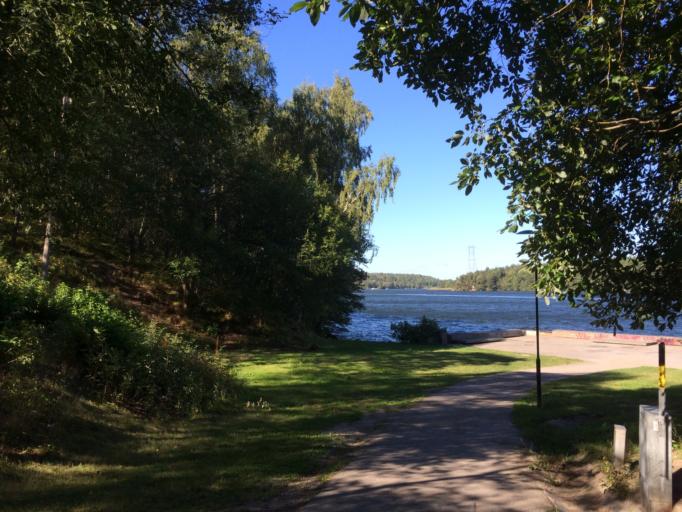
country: SE
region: Stockholm
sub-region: Huddinge Kommun
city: Segeltorp
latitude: 59.3020
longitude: 17.9349
